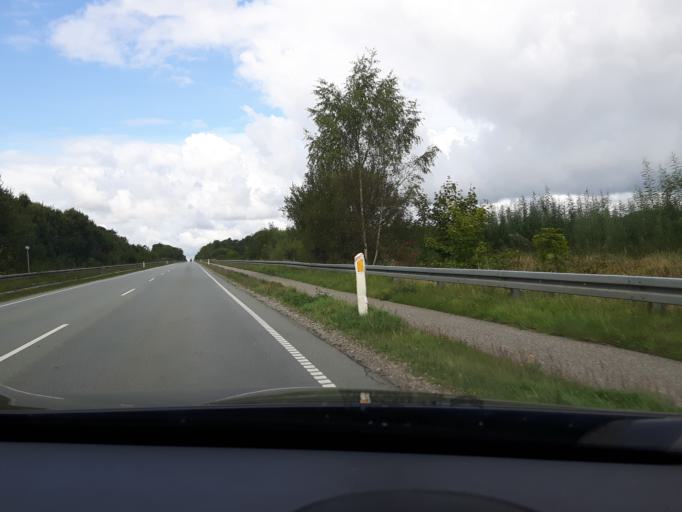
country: DK
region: Central Jutland
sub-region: Hedensted Kommune
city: Hedensted
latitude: 55.7173
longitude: 9.7326
